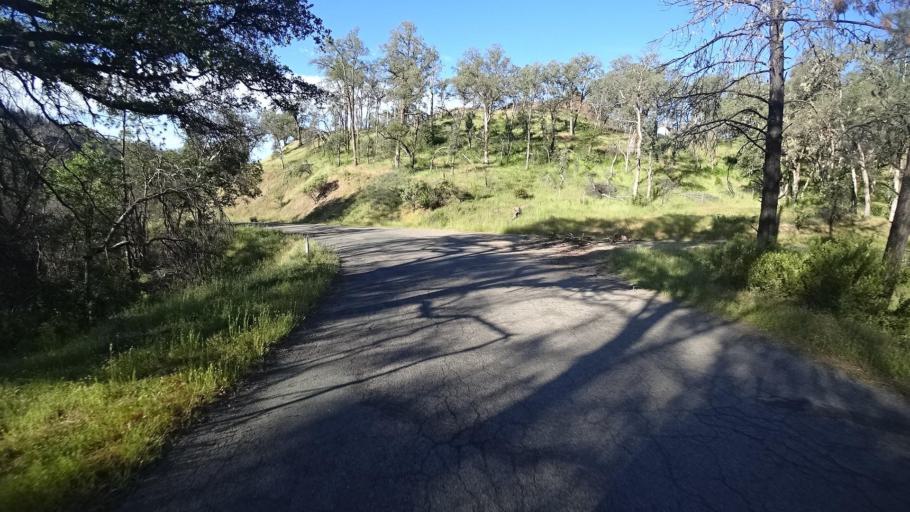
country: US
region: California
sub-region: Lake County
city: Upper Lake
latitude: 39.2581
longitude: -122.9478
